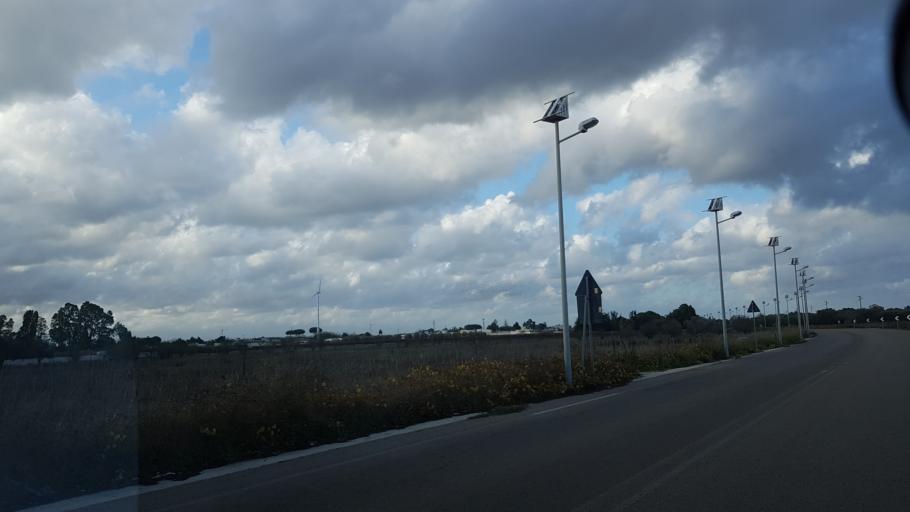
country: IT
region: Apulia
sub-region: Provincia di Brindisi
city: San Pietro Vernotico
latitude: 40.4909
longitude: 18.0098
